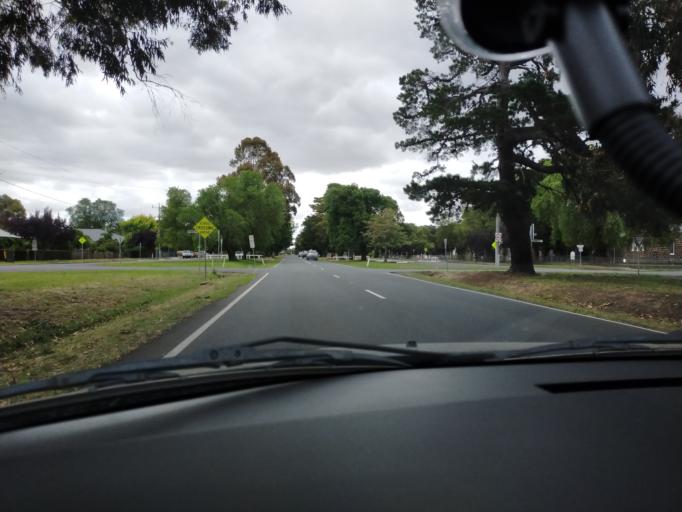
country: AU
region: Victoria
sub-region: Greater Geelong
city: Wandana Heights
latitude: -38.1011
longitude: 144.0563
